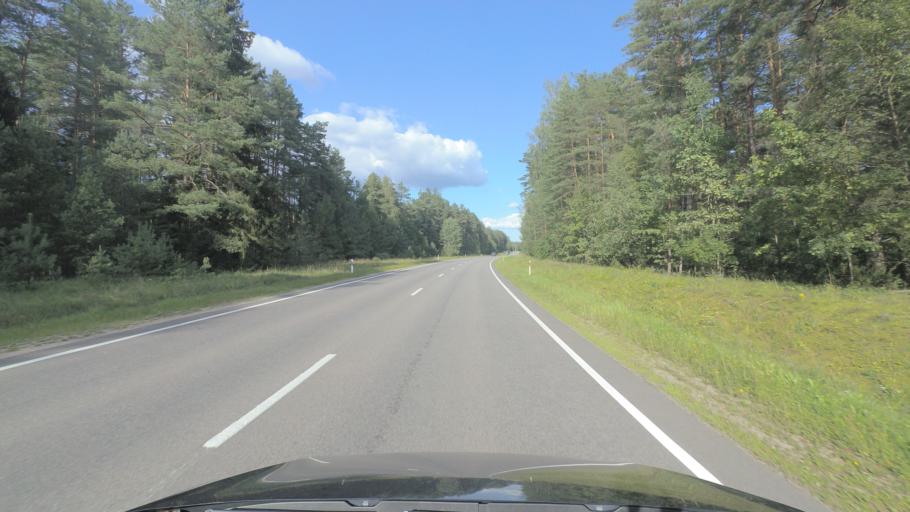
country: LT
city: Pabrade
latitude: 54.9535
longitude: 25.6722
